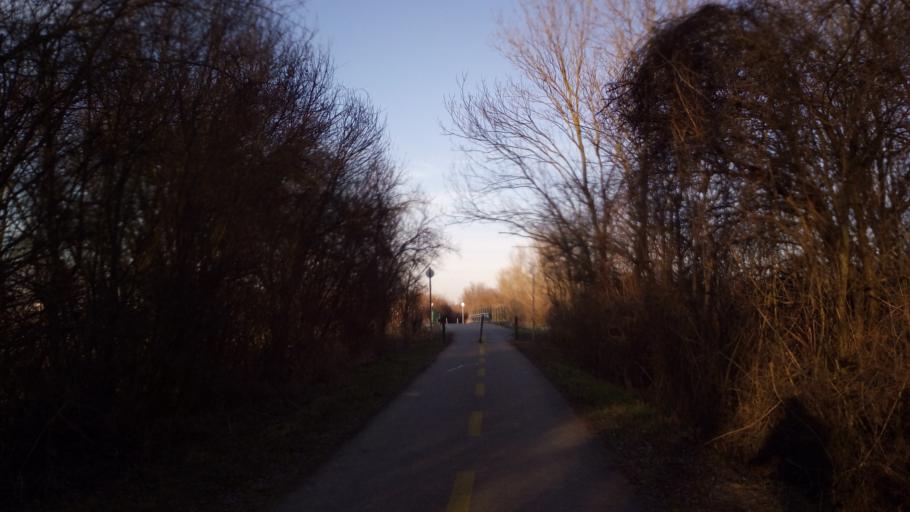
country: HU
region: Baranya
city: Pellerd
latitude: 46.0437
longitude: 18.1850
